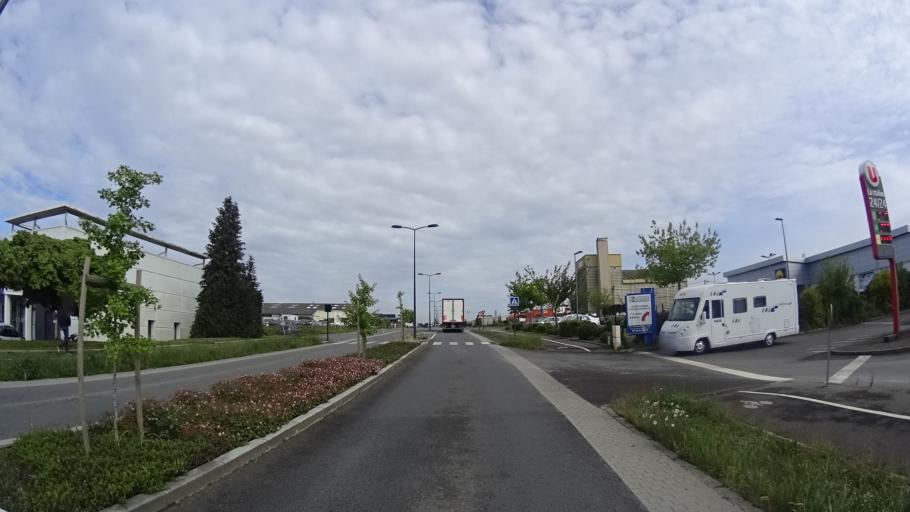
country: FR
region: Brittany
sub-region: Departement d'Ille-et-Vilaine
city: Mordelles
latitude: 48.0798
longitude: -1.8351
